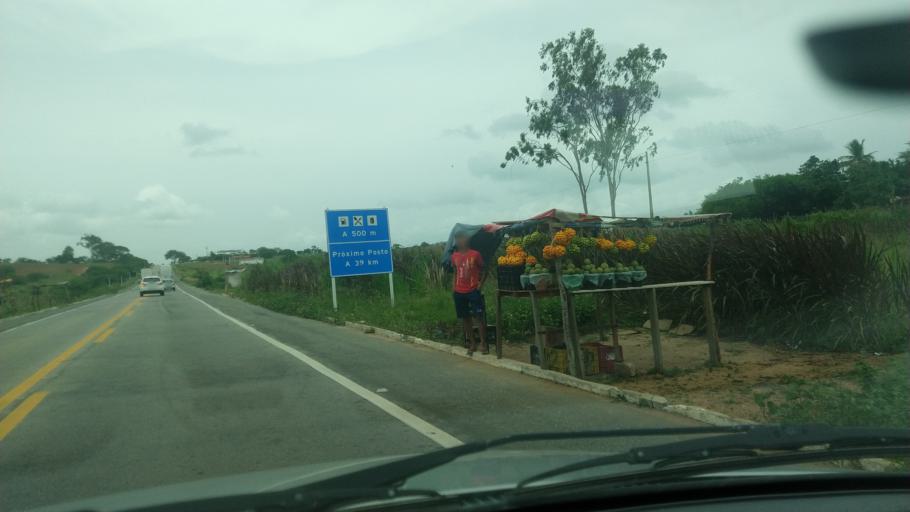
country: BR
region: Rio Grande do Norte
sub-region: Santa Cruz
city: Santa Cruz
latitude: -6.2109
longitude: -36.1821
